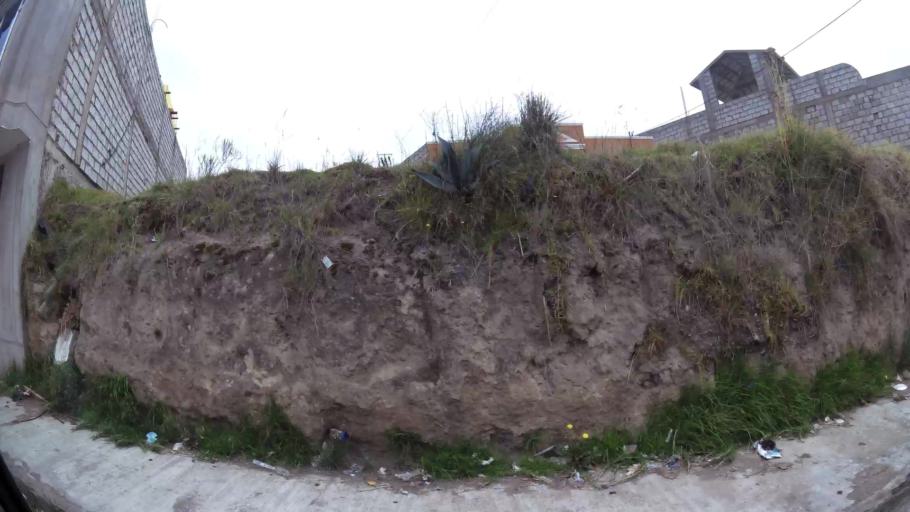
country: EC
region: Cotopaxi
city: Latacunga
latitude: -0.9560
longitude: -78.6041
